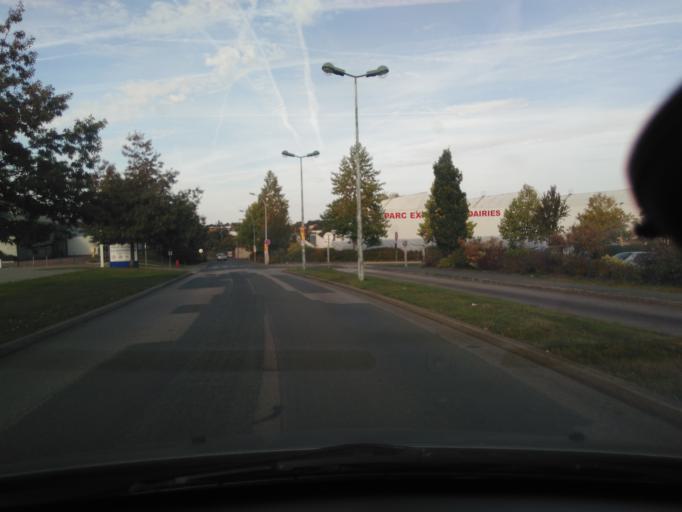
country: FR
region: Pays de la Loire
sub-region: Departement de la Vendee
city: La Roche-sur-Yon
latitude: 46.6707
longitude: -1.4061
